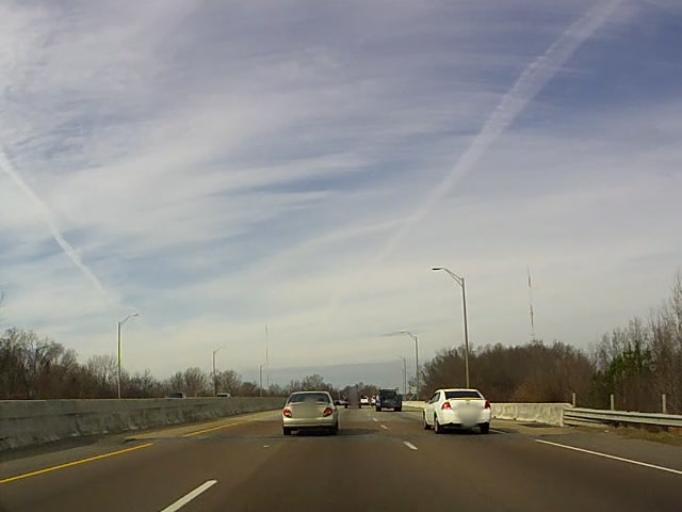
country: US
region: Tennessee
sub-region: Shelby County
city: Germantown
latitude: 35.0708
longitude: -89.8543
